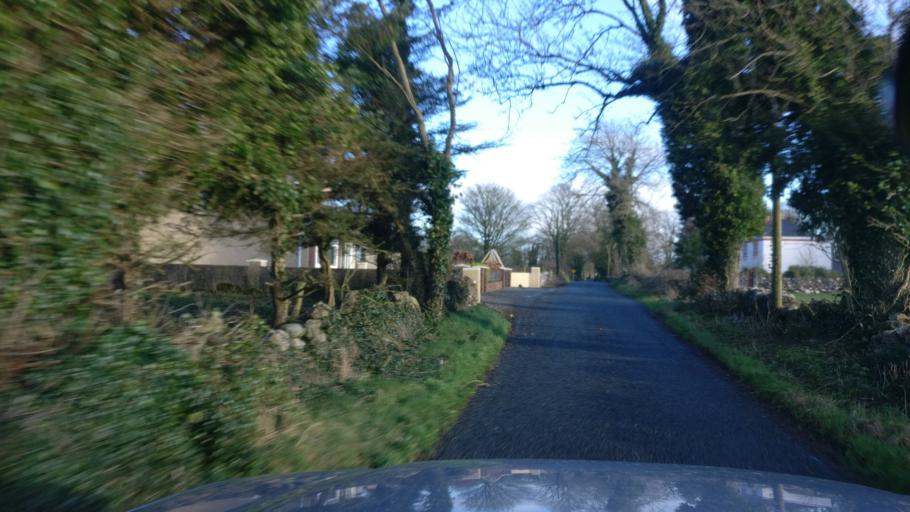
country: IE
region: Connaught
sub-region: County Galway
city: Loughrea
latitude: 53.2302
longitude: -8.5803
